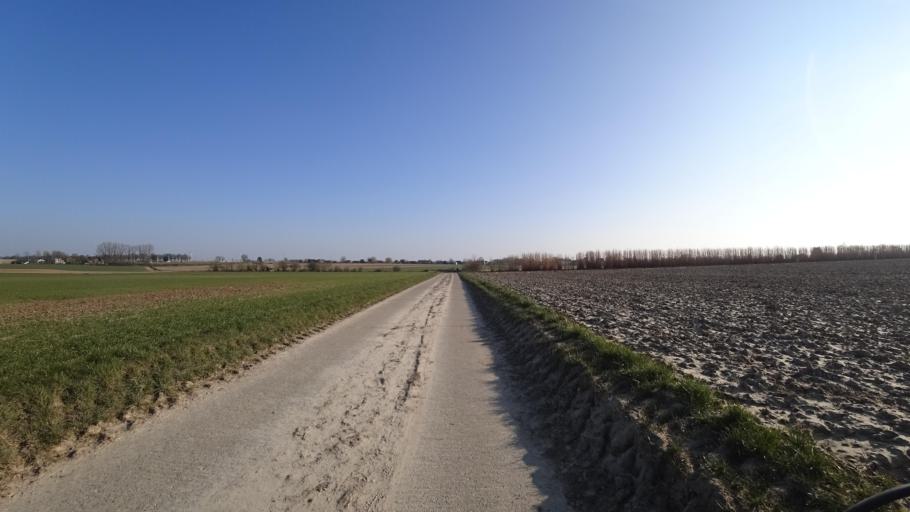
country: BE
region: Wallonia
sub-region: Province du Brabant Wallon
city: Chastre-Villeroux-Blanmont
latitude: 50.6166
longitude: 4.6559
